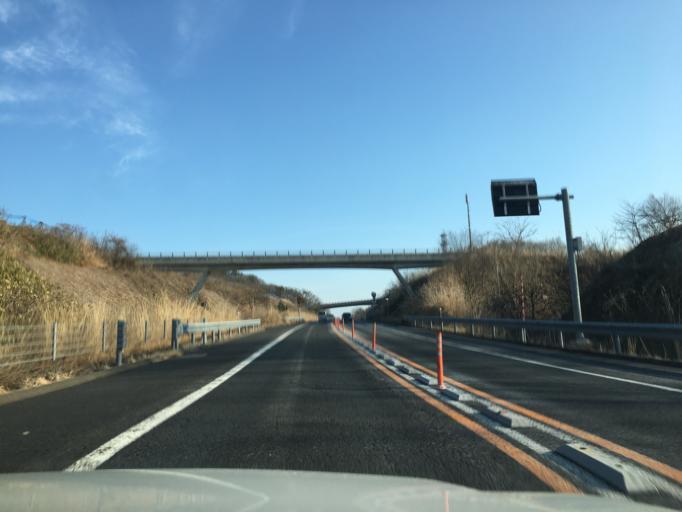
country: JP
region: Yamagata
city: Sagae
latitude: 38.3974
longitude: 140.2117
